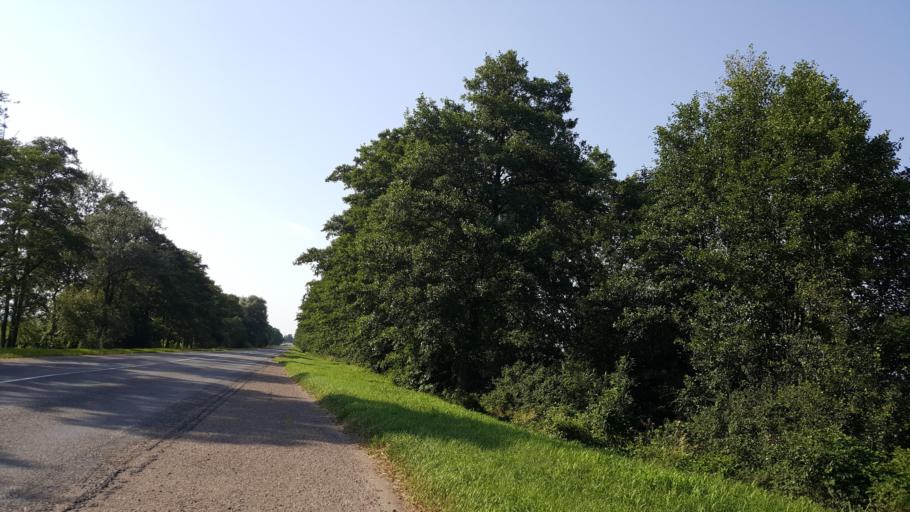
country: BY
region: Brest
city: Zhabinka
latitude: 52.3004
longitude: 23.9336
